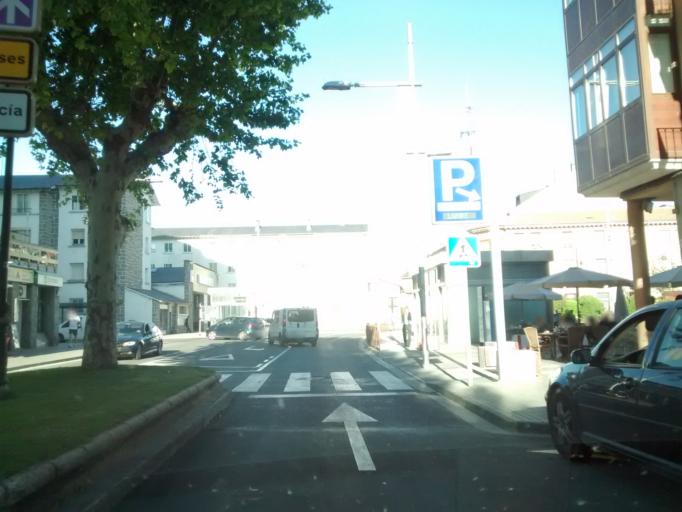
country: ES
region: Aragon
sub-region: Provincia de Huesca
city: Jaca
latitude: 42.5714
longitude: -0.5484
